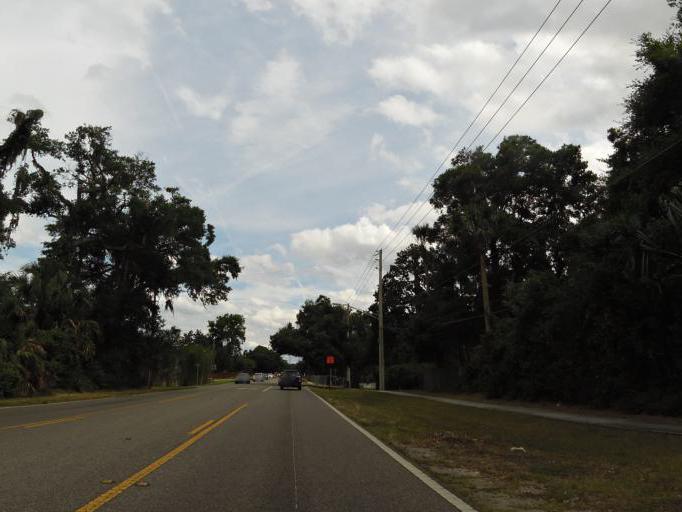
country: US
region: Florida
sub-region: Duval County
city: Neptune Beach
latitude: 30.3112
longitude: -81.4072
